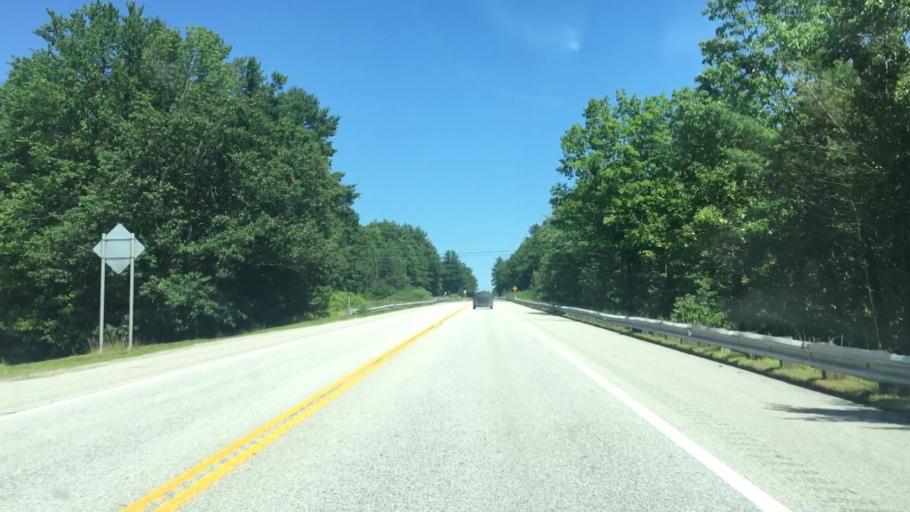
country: US
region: New Hampshire
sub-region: Merrimack County
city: Hopkinton
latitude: 43.1778
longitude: -71.6925
